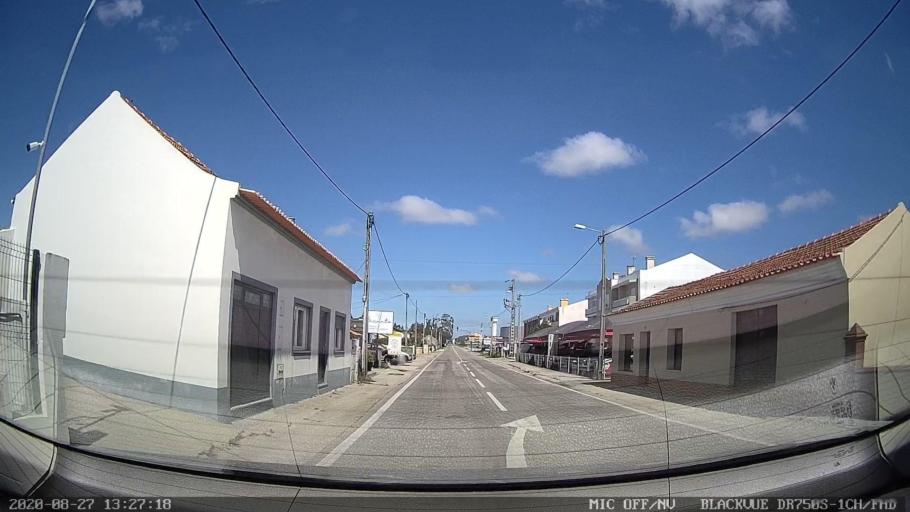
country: PT
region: Aveiro
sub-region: Vagos
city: Vagos
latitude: 40.5318
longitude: -8.6782
